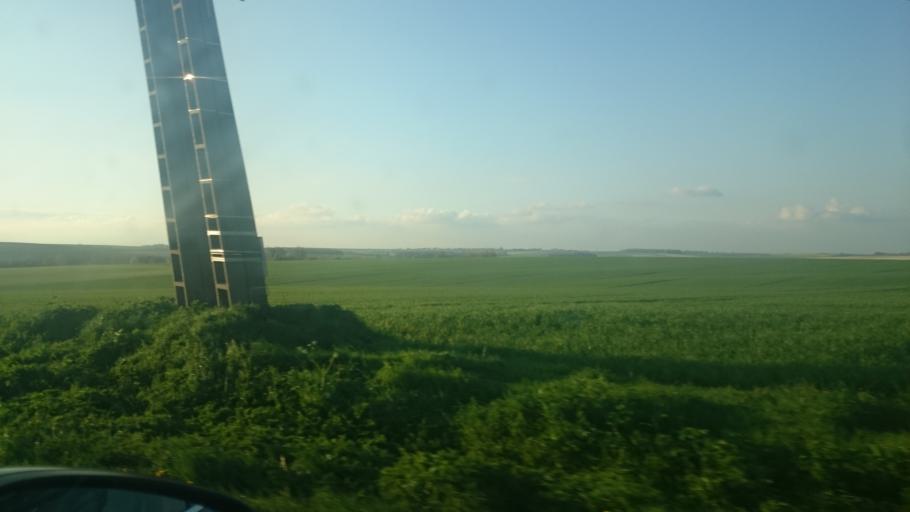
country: FR
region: Picardie
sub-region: Departement de l'Aisne
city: Ribemont
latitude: 49.8401
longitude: 3.4534
